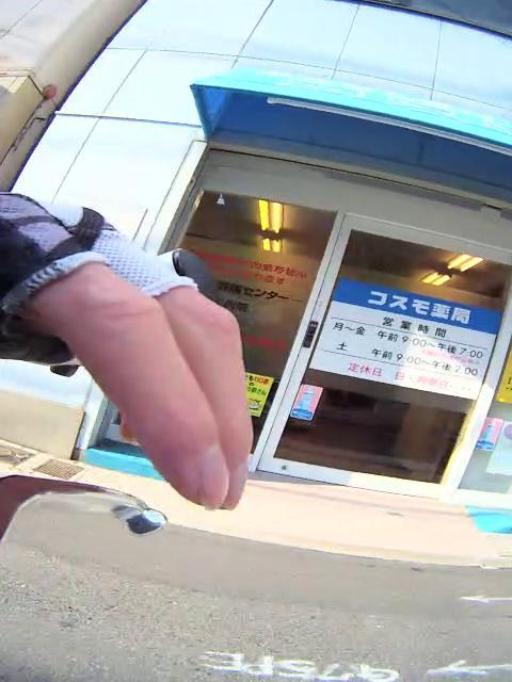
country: JP
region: Osaka
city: Suita
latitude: 34.7359
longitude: 135.4839
